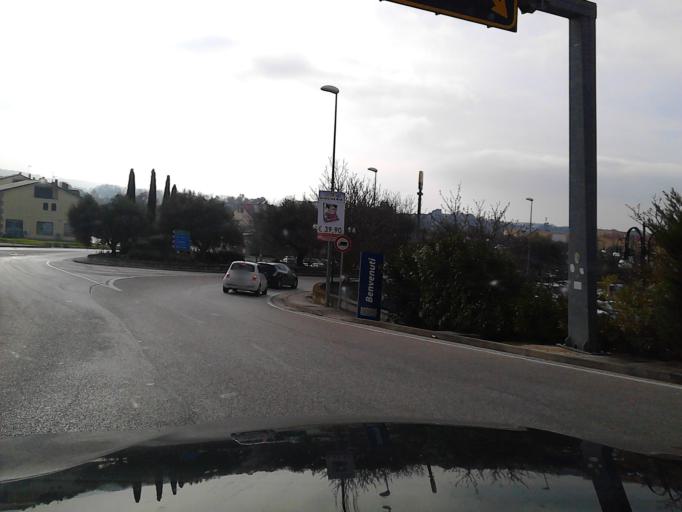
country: IT
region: Abruzzo
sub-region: Provincia di Teramo
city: Villa Rosa
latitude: 42.8368
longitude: 13.8951
